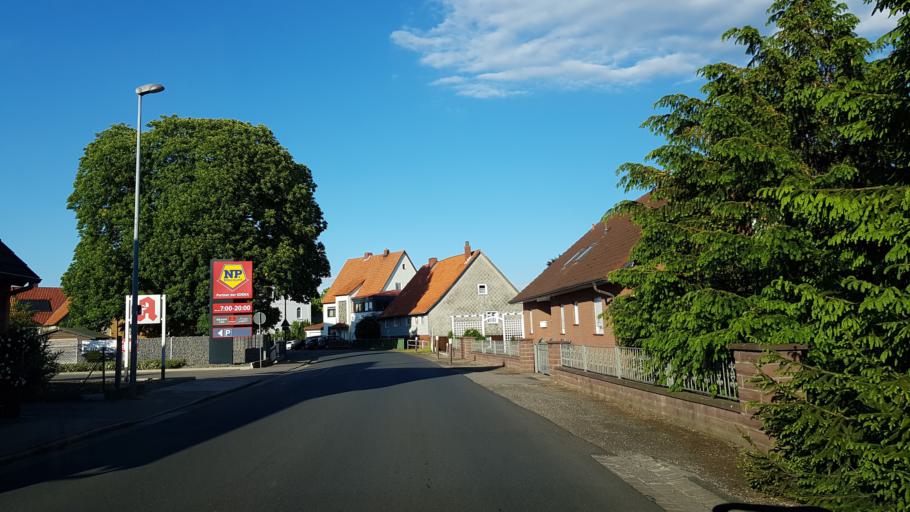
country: DE
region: Lower Saxony
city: Nordstemmen
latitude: 52.1955
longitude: 9.7804
